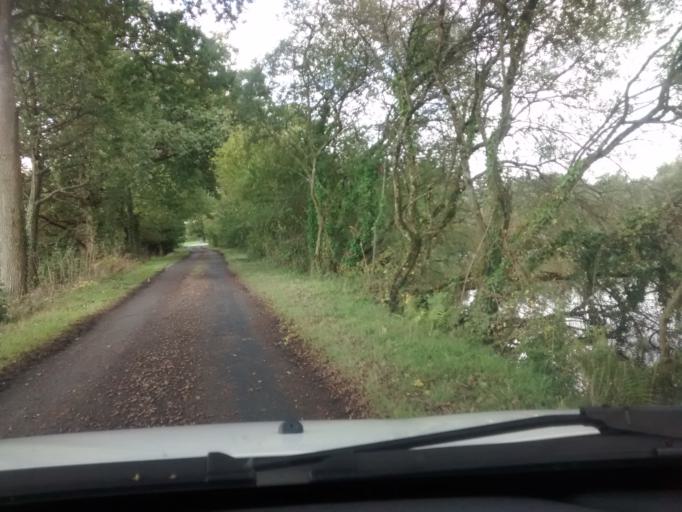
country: FR
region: Brittany
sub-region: Departement d'Ille-et-Vilaine
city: Chateaubourg
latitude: 48.1348
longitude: -1.4228
